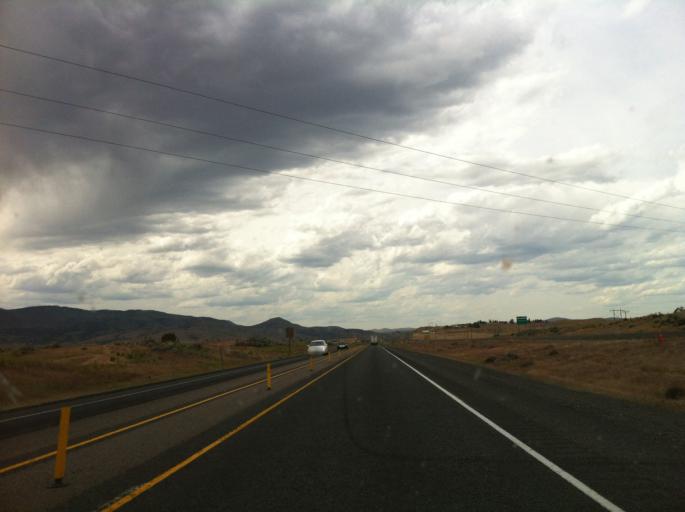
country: US
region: Oregon
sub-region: Baker County
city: Baker City
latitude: 44.5590
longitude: -117.4282
